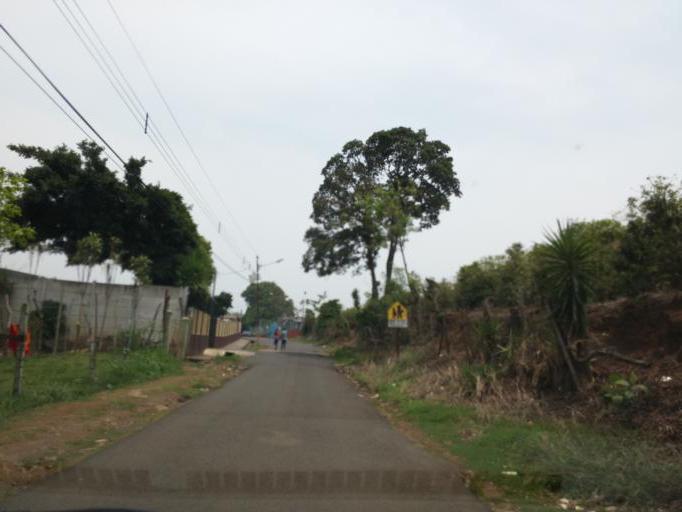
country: CR
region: Heredia
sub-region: Canton de Belen
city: San Antonio
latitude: 9.9926
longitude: -84.2002
